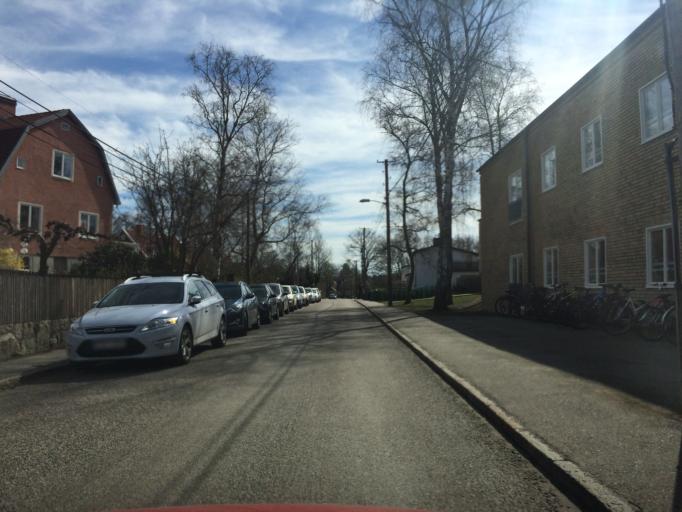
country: SE
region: Stockholm
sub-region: Huddinge Kommun
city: Huddinge
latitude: 59.2776
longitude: 17.9832
